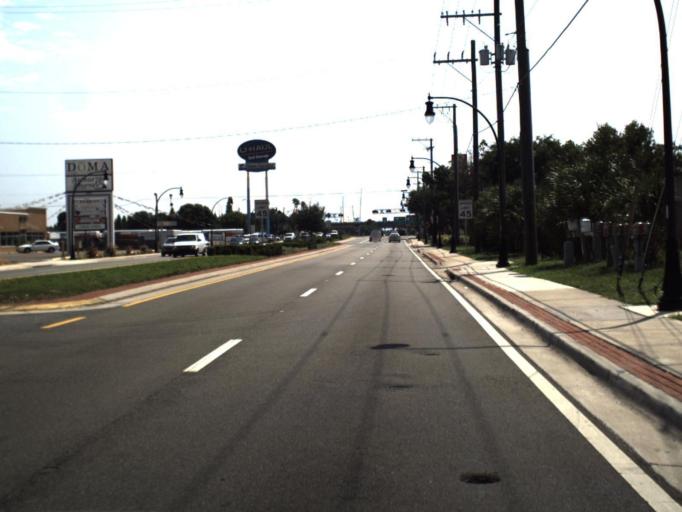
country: US
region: Florida
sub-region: Hillsborough County
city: Tampa
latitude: 27.8937
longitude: -82.5123
